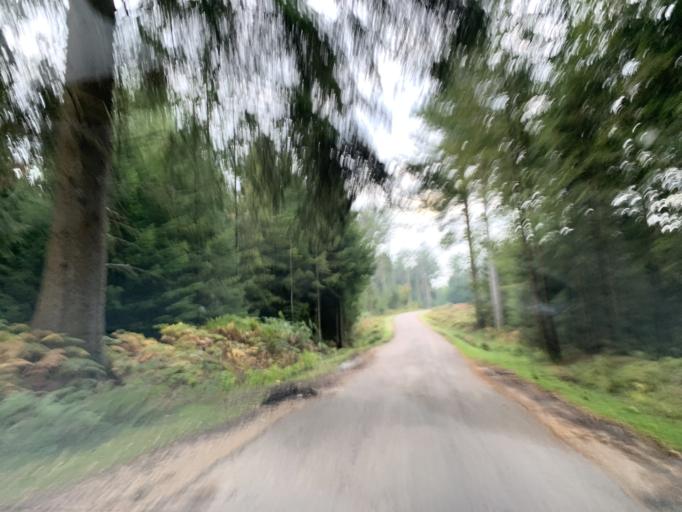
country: GB
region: England
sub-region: Hampshire
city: Lyndhurst
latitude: 50.8580
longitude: -1.6325
